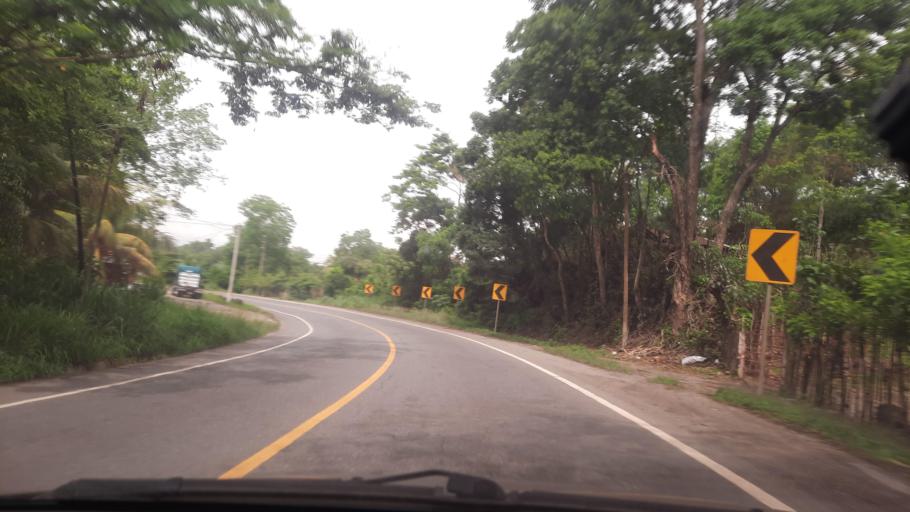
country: GT
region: Izabal
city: Morales
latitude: 15.5225
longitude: -88.7956
